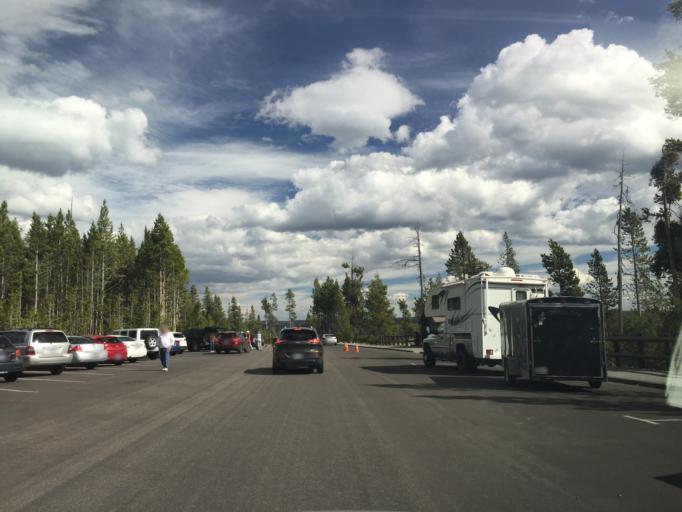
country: US
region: Montana
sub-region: Gallatin County
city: West Yellowstone
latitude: 44.7197
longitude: -110.4969
